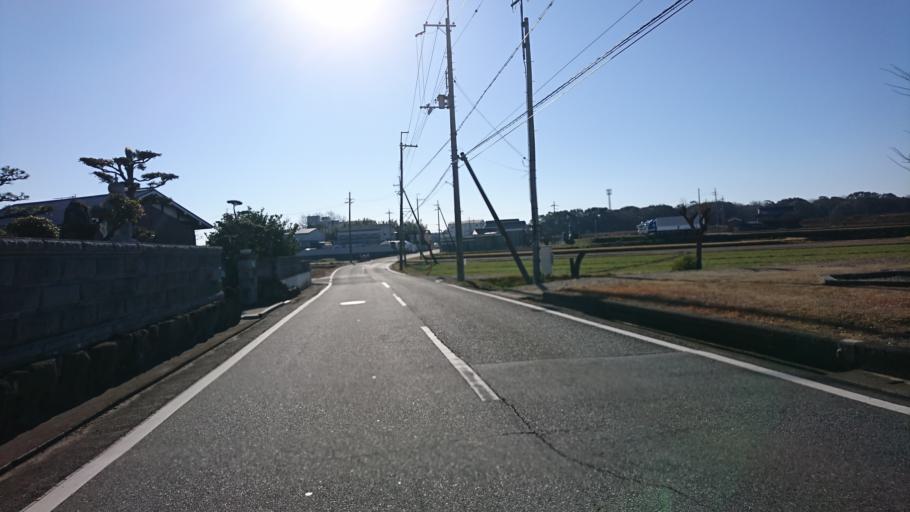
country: JP
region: Hyogo
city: Miki
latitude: 34.7584
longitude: 134.9247
